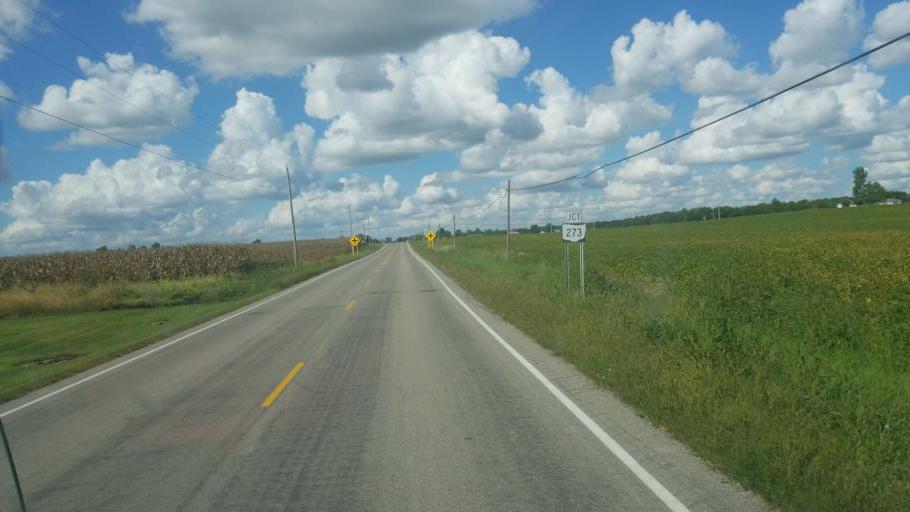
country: US
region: Ohio
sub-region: Hardin County
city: Kenton
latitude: 40.5256
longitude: -83.5750
